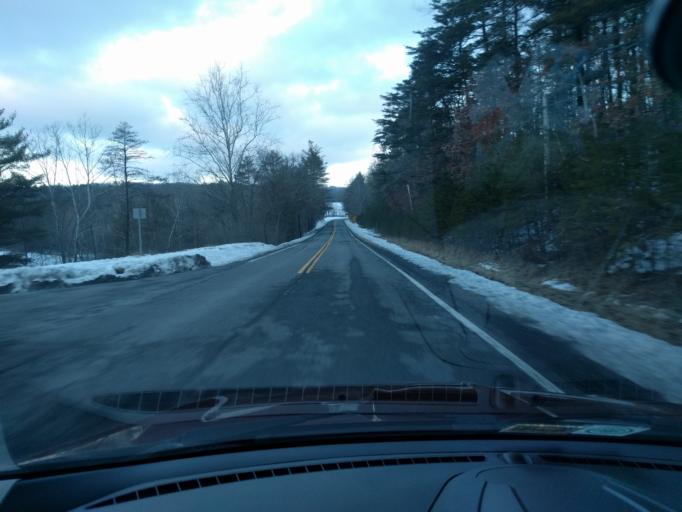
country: US
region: Virginia
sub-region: Bath County
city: Warm Springs
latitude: 38.0628
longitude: -79.8270
